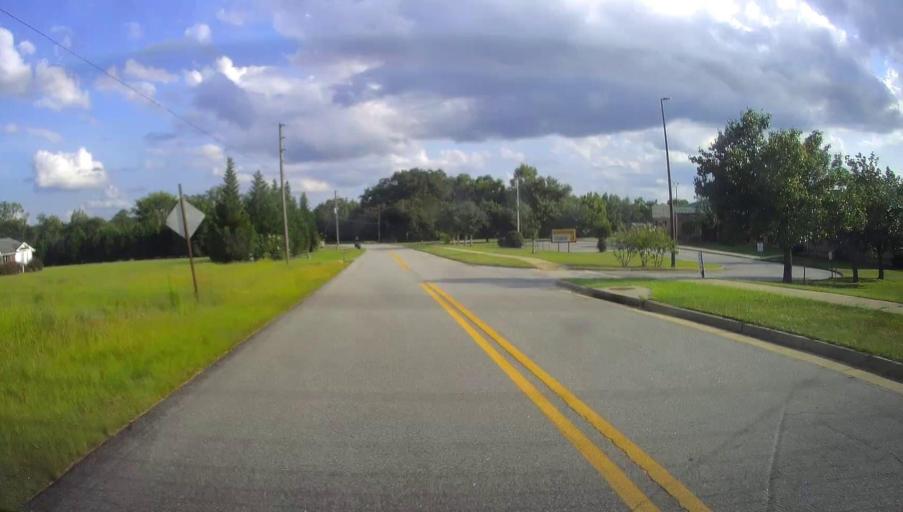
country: US
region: Georgia
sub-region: Crawford County
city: Roberta
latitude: 32.7289
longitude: -84.0065
